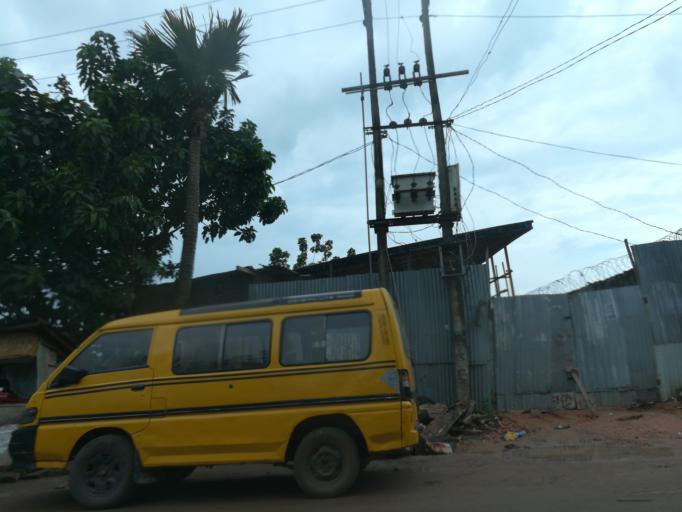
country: NG
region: Lagos
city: Agege
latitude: 6.6090
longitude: 3.3235
